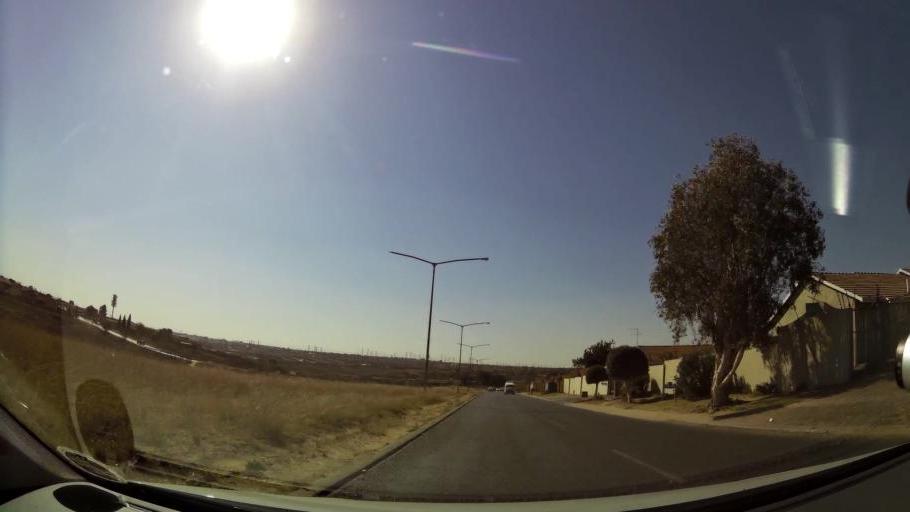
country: ZA
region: Gauteng
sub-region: Ekurhuleni Metropolitan Municipality
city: Tembisa
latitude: -26.0440
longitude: 28.2187
